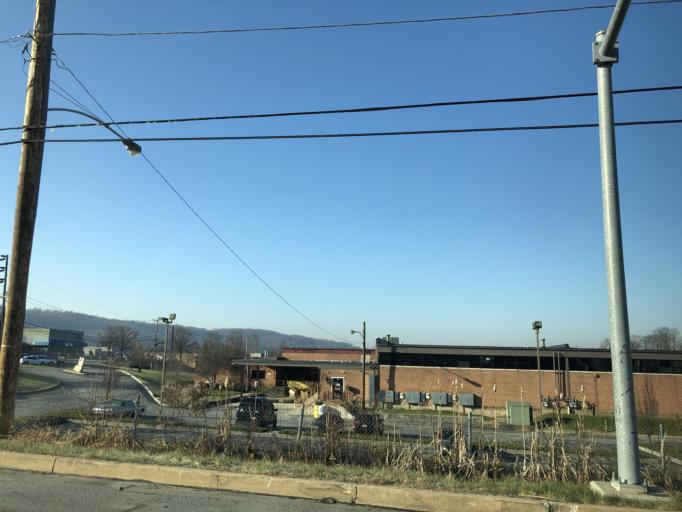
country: US
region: Pennsylvania
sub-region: Chester County
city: Downingtown
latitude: 40.0022
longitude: -75.6940
